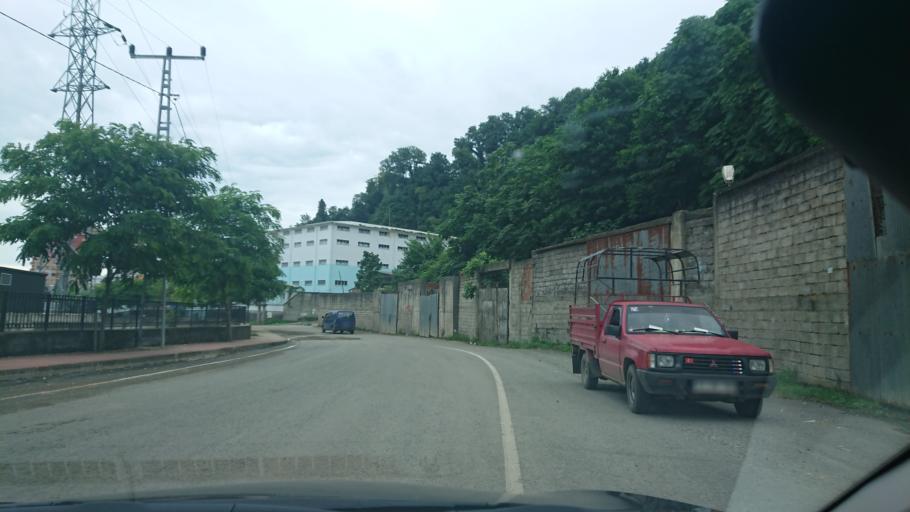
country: TR
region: Rize
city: Rize
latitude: 41.0313
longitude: 40.4830
